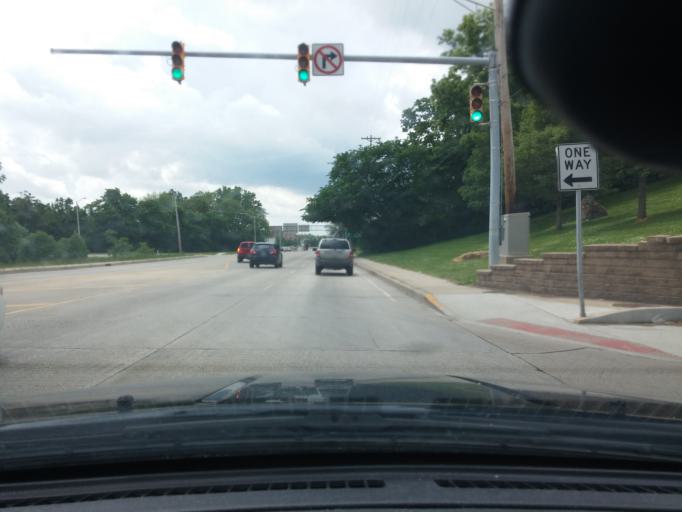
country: US
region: Indiana
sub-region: Tippecanoe County
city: West Lafayette
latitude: 40.4257
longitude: -86.9023
